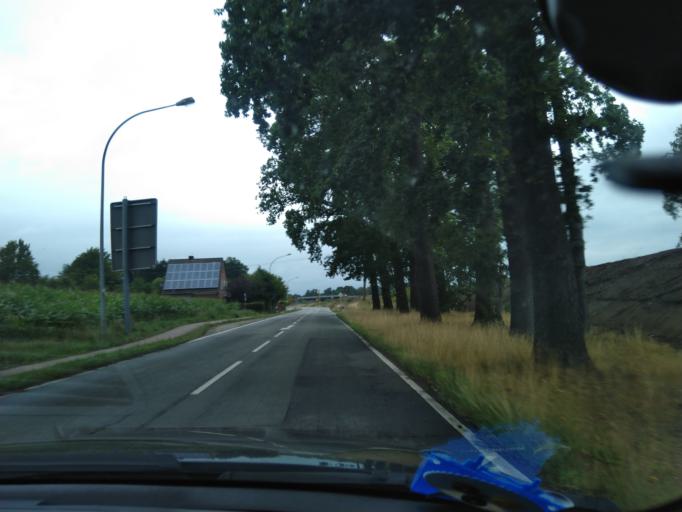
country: DE
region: Lower Saxony
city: Nordhorn
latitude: 52.4457
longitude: 7.0863
